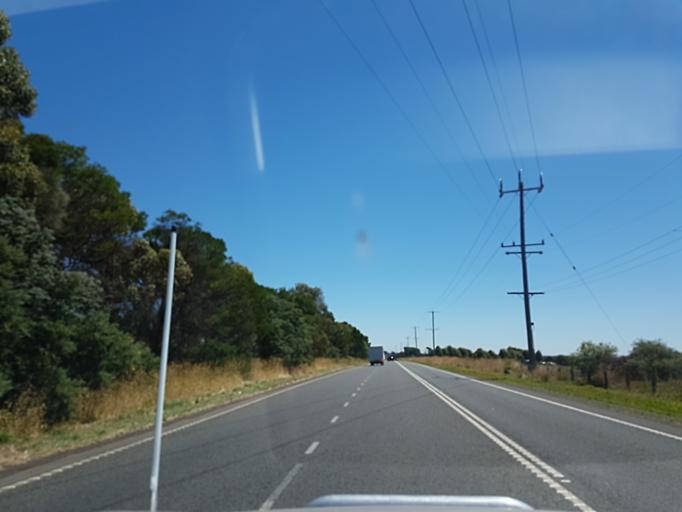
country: AU
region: Victoria
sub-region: Colac-Otway
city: Colac
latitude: -38.3414
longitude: 143.4792
